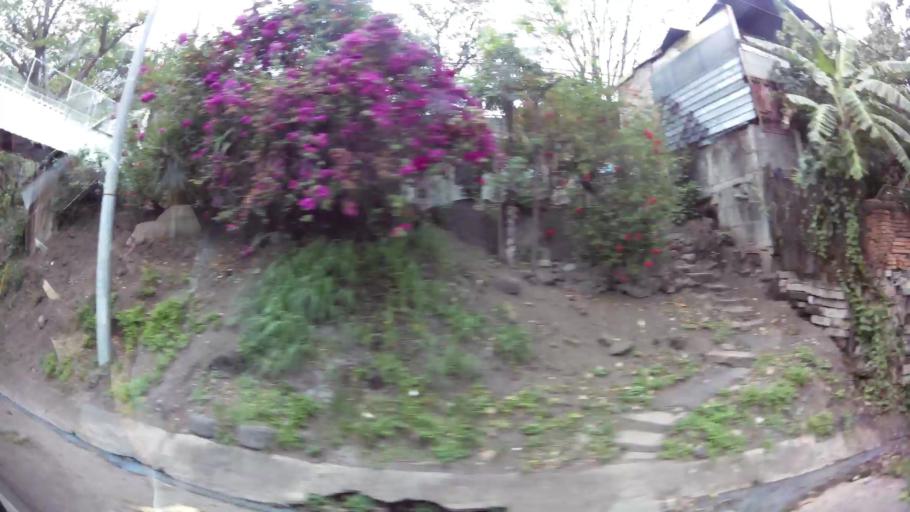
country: NI
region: Matagalpa
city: Matagalpa
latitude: 12.9320
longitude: -85.9212
